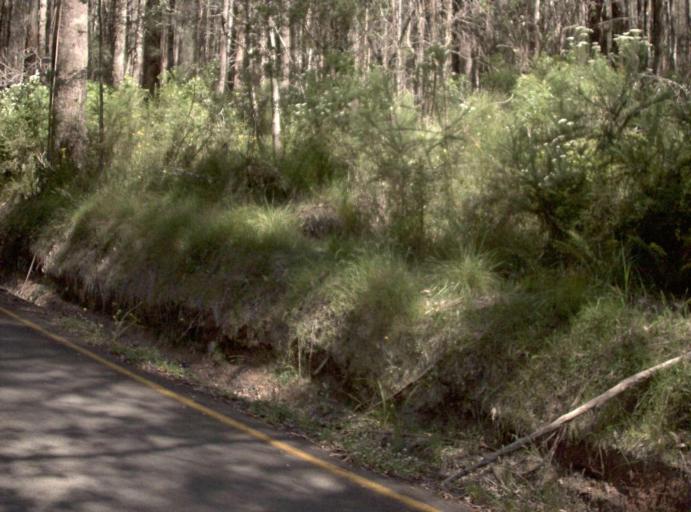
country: AU
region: Victoria
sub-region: Yarra Ranges
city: Millgrove
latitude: -37.5403
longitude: 145.8439
